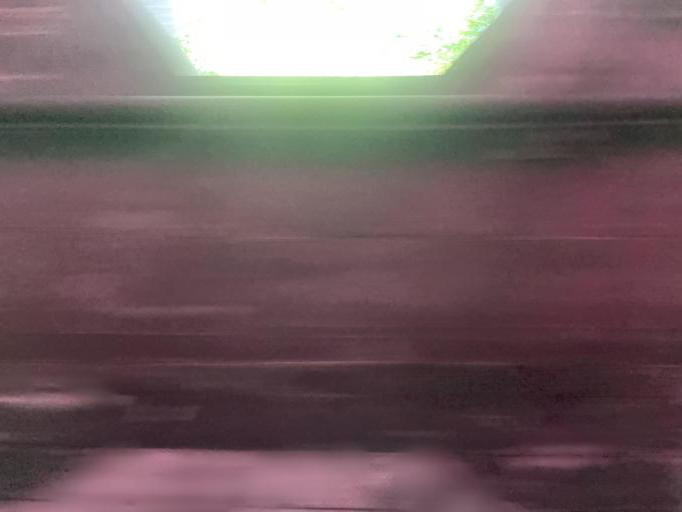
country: JP
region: Niigata
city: Murakami
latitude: 38.3538
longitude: 139.4517
